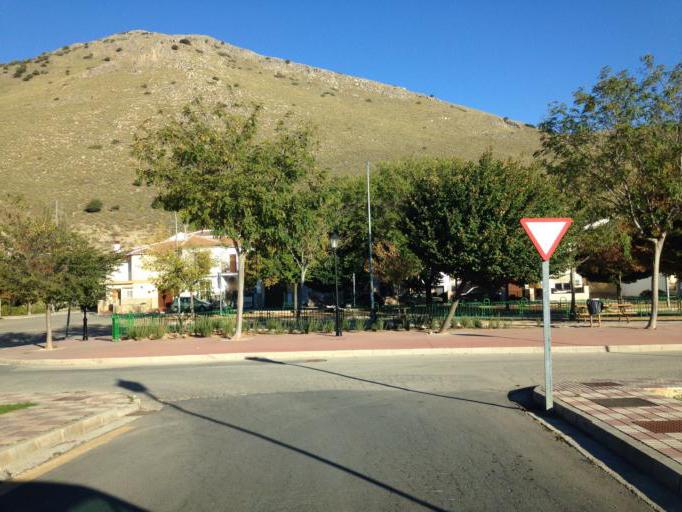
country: ES
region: Andalusia
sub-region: Provincia de Malaga
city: Archidona
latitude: 37.0966
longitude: -4.3737
